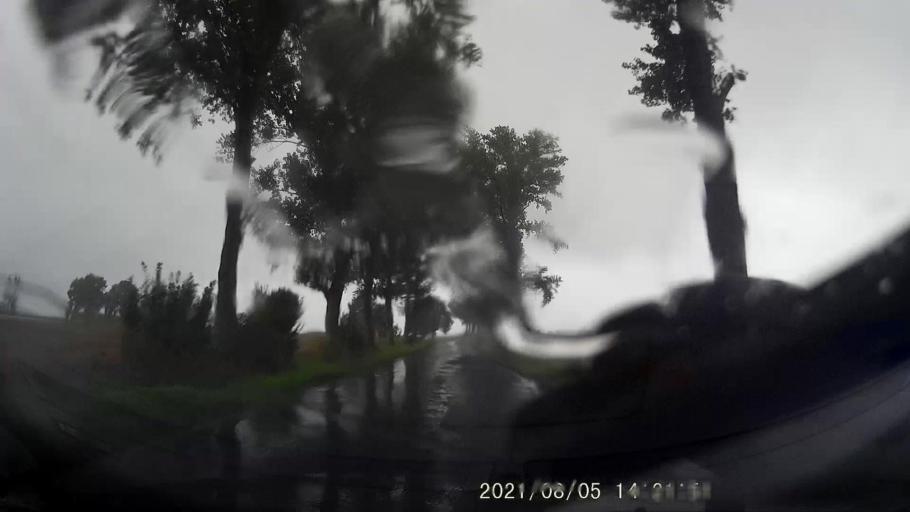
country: PL
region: Opole Voivodeship
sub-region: Powiat nyski
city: Korfantow
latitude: 50.4726
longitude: 17.6662
